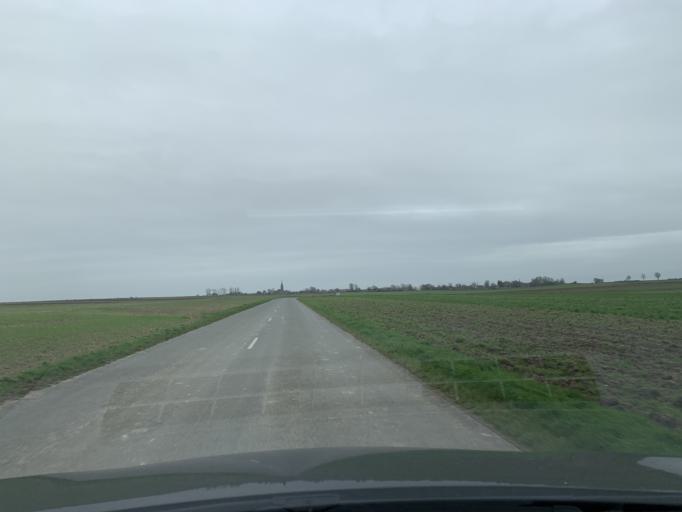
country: FR
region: Nord-Pas-de-Calais
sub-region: Departement du Pas-de-Calais
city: Oisy-le-Verger
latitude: 50.2399
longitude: 3.1480
